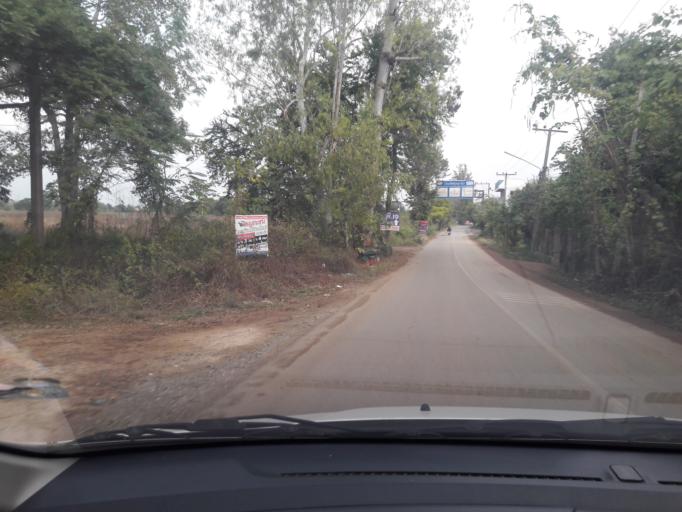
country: TH
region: Chiang Mai
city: Saraphi
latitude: 18.7137
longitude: 99.0455
